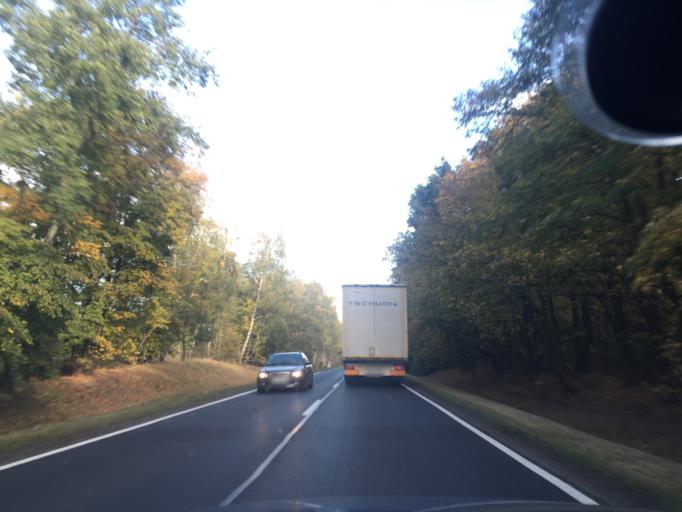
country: PL
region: Kujawsko-Pomorskie
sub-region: Powiat mogilenski
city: Strzelno
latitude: 52.6257
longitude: 18.0983
